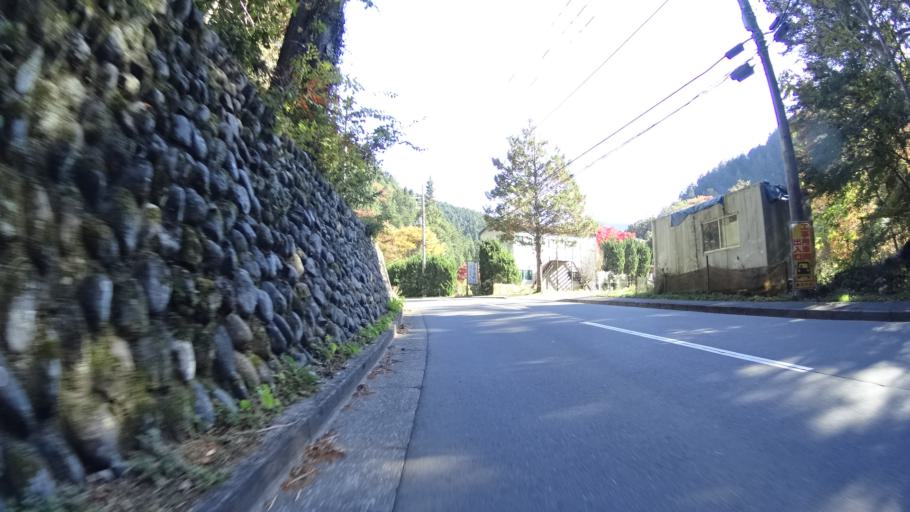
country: JP
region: Yamanashi
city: Uenohara
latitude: 35.7076
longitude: 139.0968
